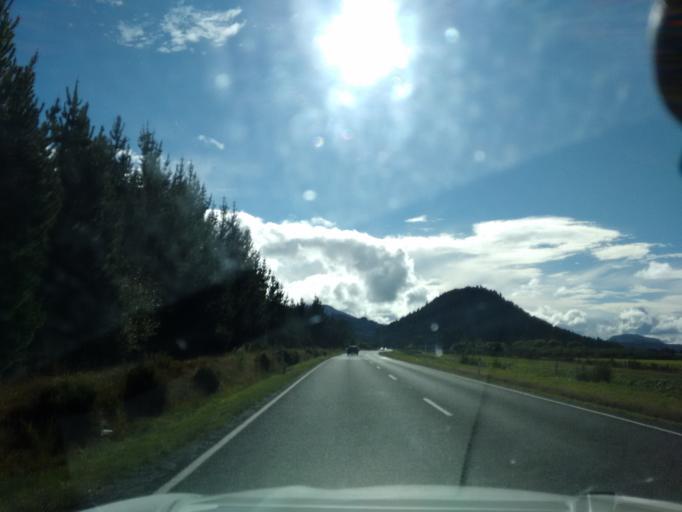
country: NZ
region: Waikato
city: Turangi
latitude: -38.9842
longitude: 175.7829
